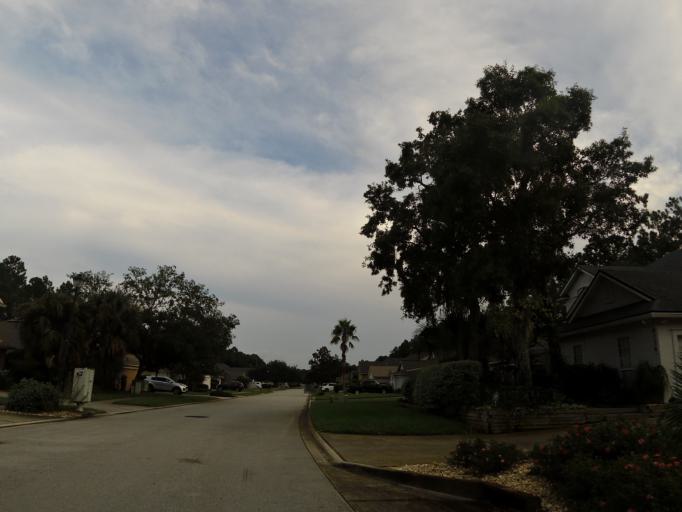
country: US
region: Florida
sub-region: Saint Johns County
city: Palm Valley
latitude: 30.2109
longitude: -81.5179
